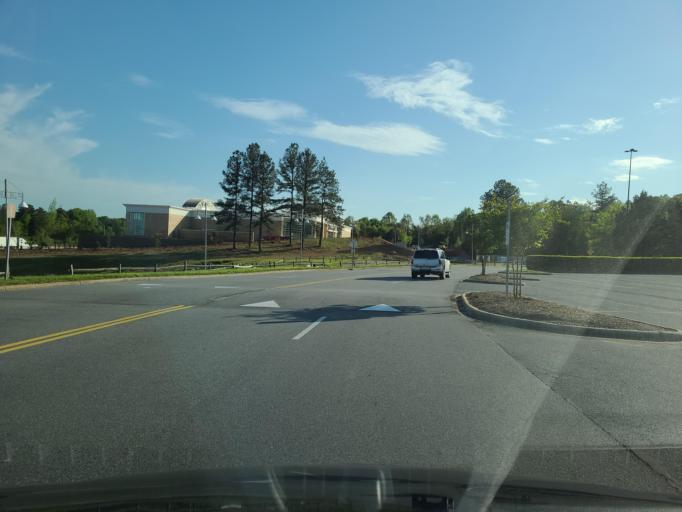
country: US
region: North Carolina
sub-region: Cabarrus County
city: Harrisburg
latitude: 35.3665
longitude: -80.7181
